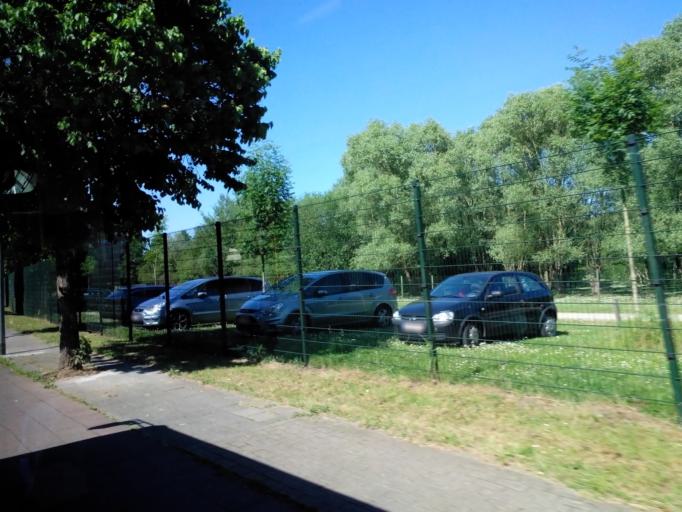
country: BE
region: Flanders
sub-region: Provincie Vlaams-Brabant
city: Leuven
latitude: 50.8956
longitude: 4.7169
